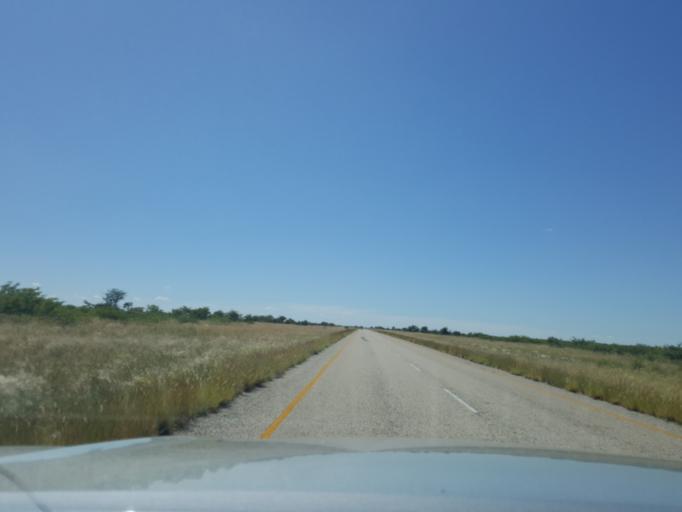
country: BW
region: Central
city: Gweta
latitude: -20.2310
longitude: 24.9622
